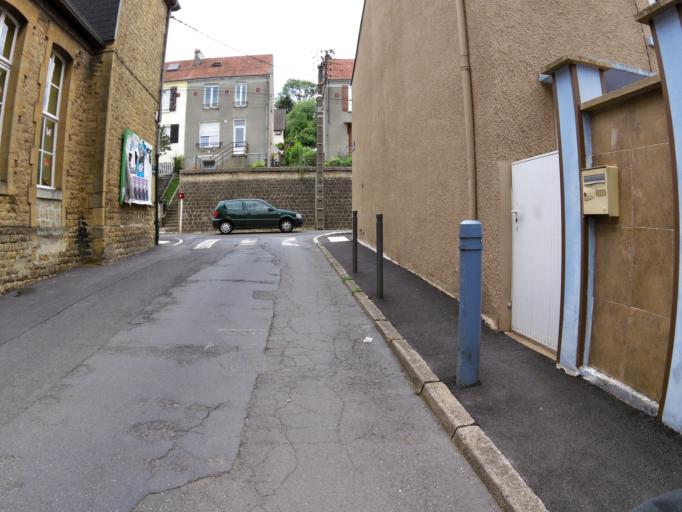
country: FR
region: Champagne-Ardenne
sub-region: Departement des Ardennes
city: Montcy-Notre-Dame
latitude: 49.7582
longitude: 4.7395
